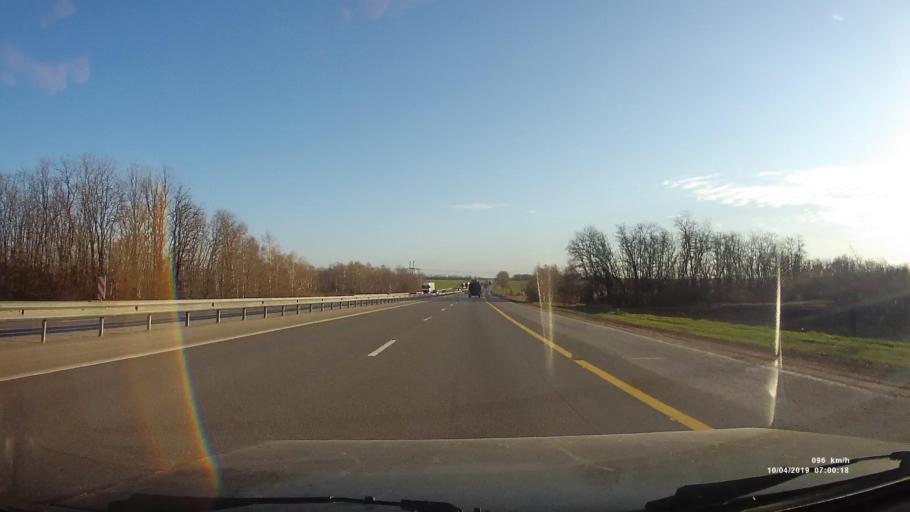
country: RU
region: Rostov
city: Krasyukovskaya
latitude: 47.5794
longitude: 39.9719
